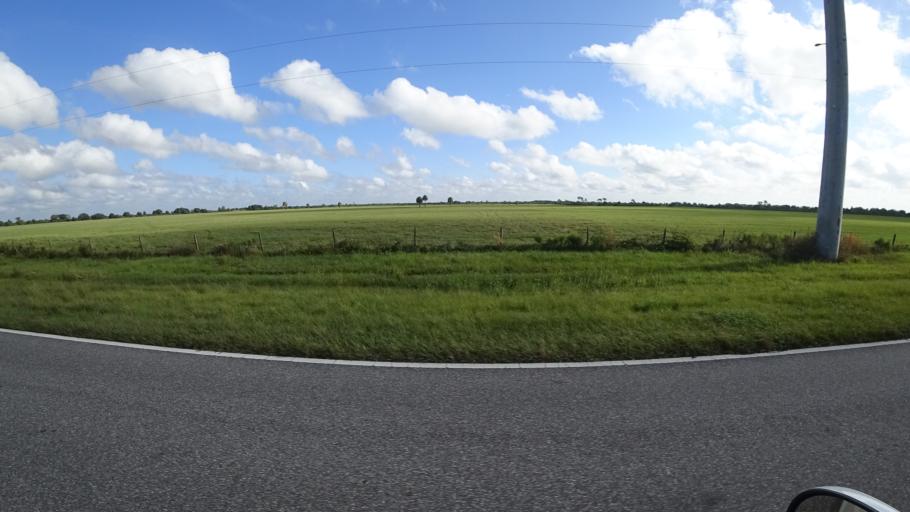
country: US
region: Florida
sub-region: Hillsborough County
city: Wimauma
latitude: 27.5234
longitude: -82.3313
